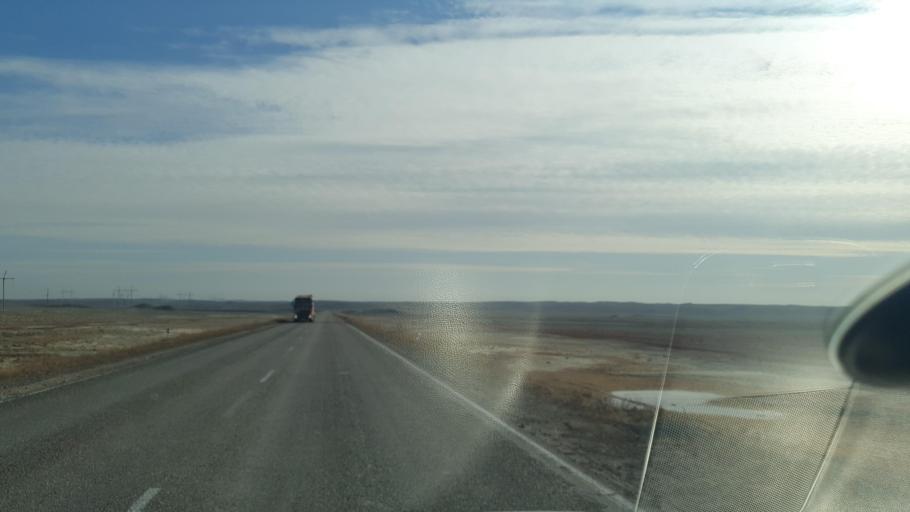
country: KZ
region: Zhambyl
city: Mynaral
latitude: 45.5733
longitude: 73.4150
